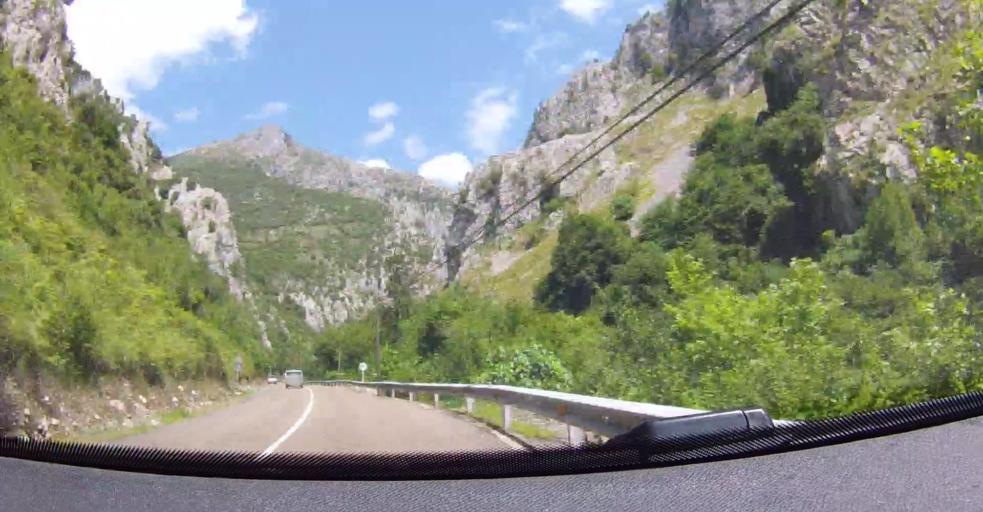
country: ES
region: Cantabria
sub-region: Provincia de Cantabria
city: Tresviso
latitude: 43.2825
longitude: -4.6267
